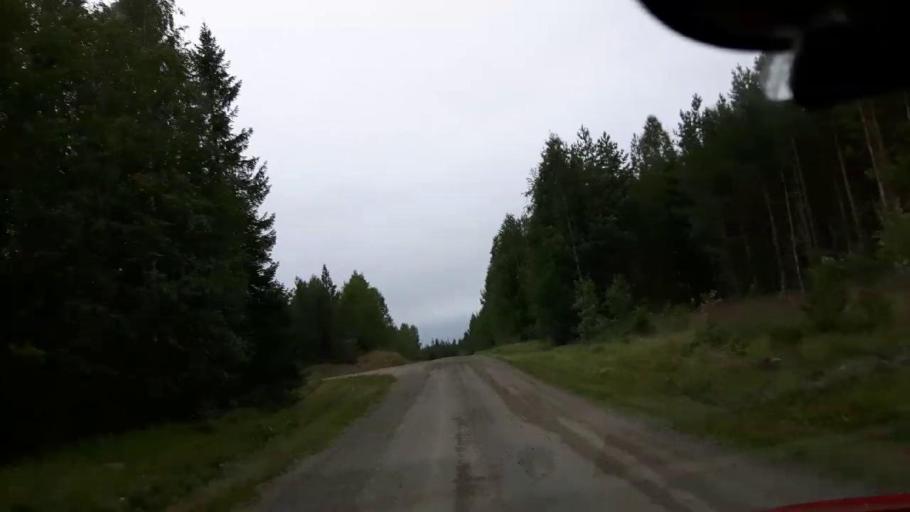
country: SE
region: Vaesternorrland
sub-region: Ange Kommun
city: Fransta
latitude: 62.8536
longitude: 15.9722
